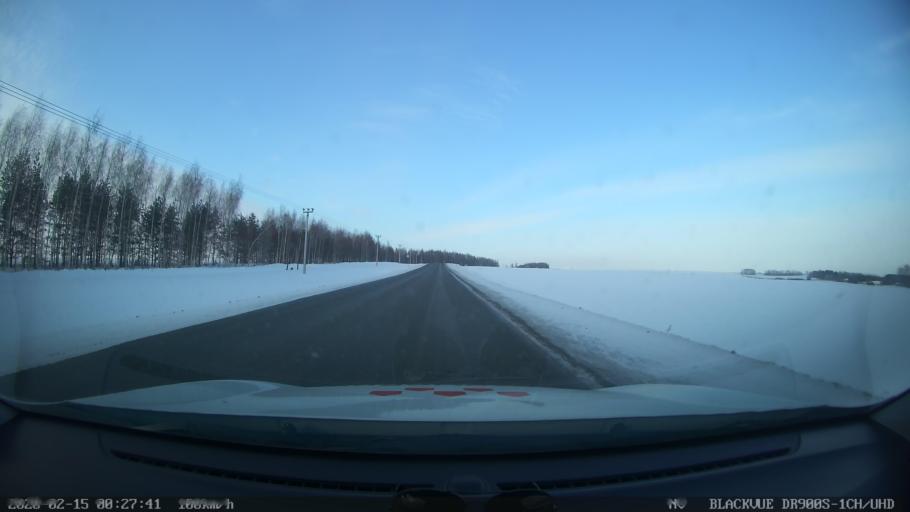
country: RU
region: Tatarstan
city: Verkhniy Uslon
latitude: 55.6325
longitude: 48.8730
